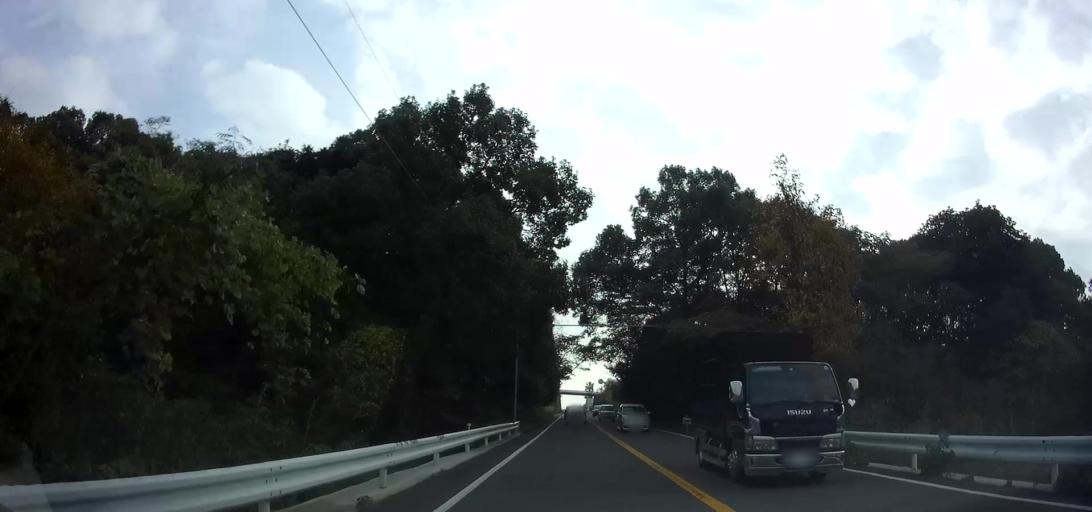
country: JP
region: Nagasaki
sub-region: Isahaya-shi
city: Isahaya
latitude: 32.7961
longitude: 130.0946
